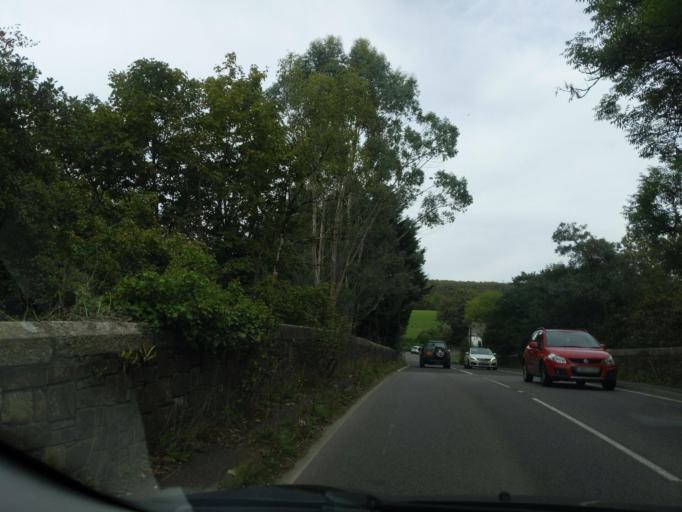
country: GB
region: England
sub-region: Cornwall
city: Bodmin
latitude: 50.4774
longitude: -4.7528
